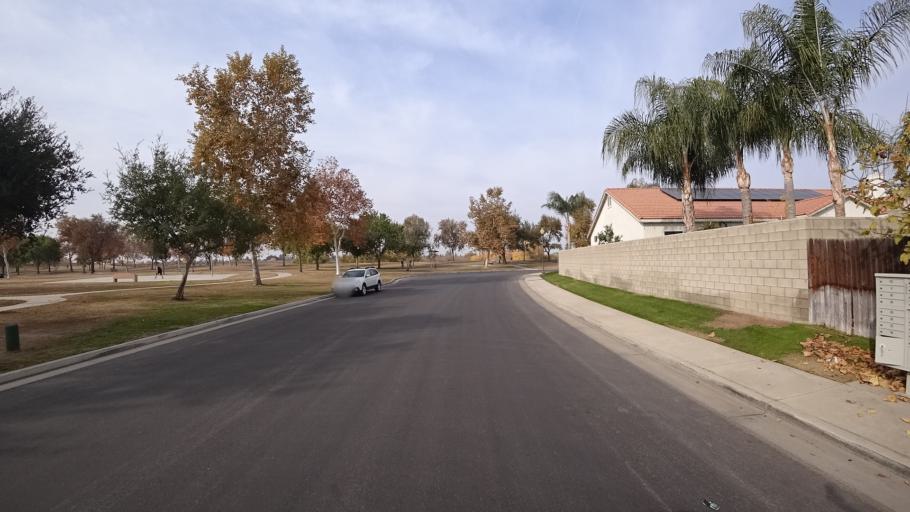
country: US
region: California
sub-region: Kern County
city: Rosedale
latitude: 35.3443
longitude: -119.1422
